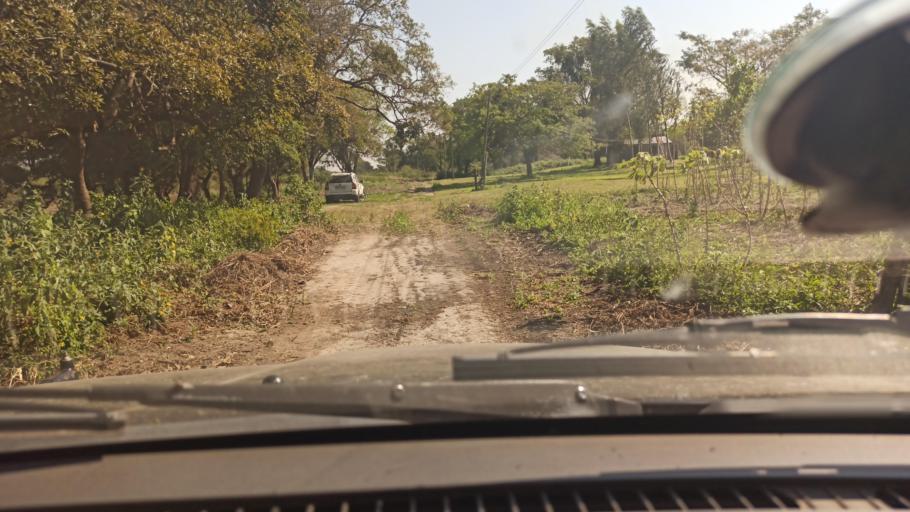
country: PY
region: Asuncion
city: Asuncion
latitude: -25.3530
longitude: -57.6679
